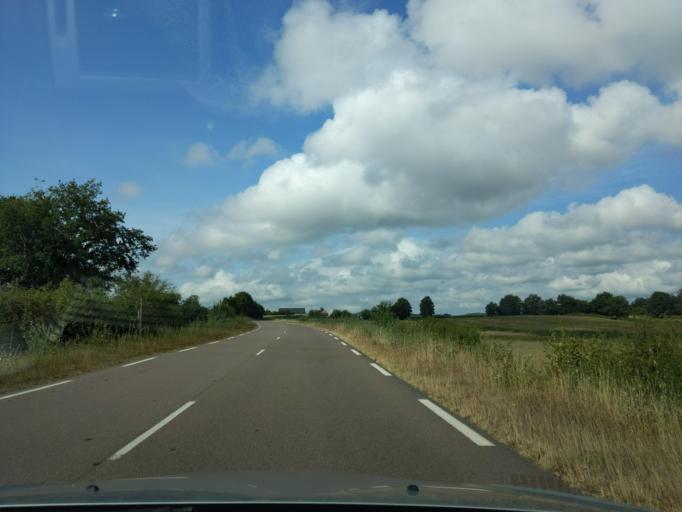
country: FR
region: Bourgogne
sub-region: Departement de Saone-et-Loire
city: Etang-sur-Arroux
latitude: 46.8642
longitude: 4.1144
